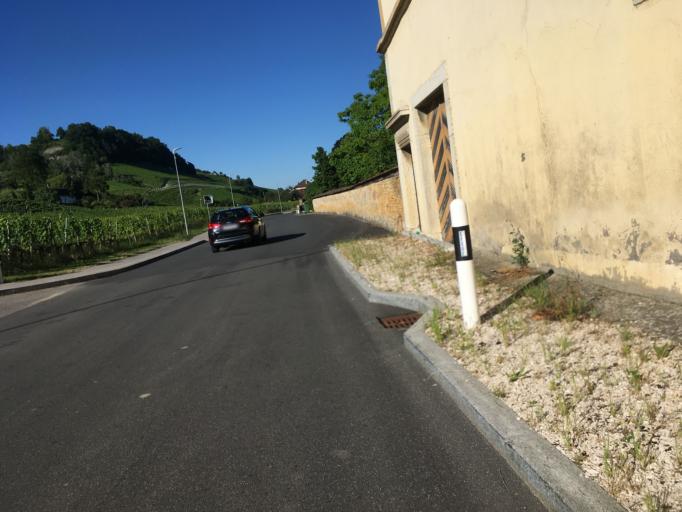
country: CH
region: Fribourg
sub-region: See District
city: Bas-Vully
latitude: 46.9521
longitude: 7.0929
